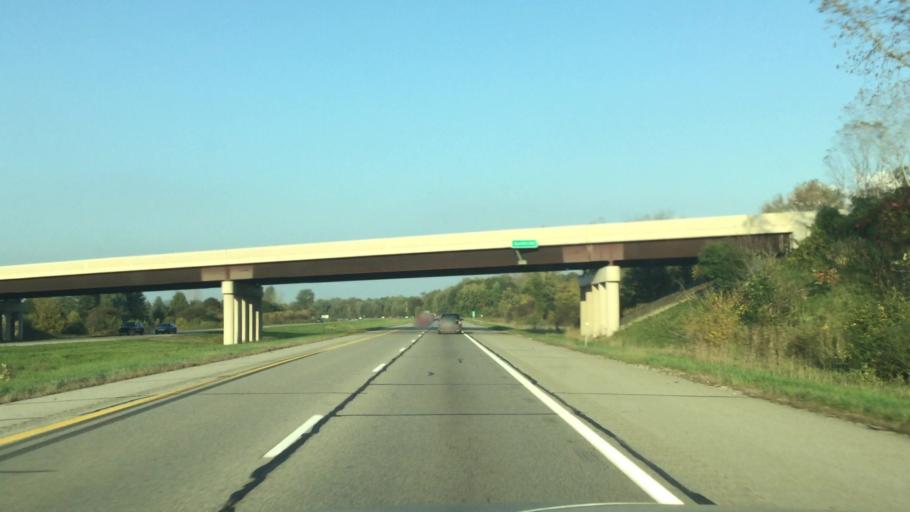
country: US
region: Michigan
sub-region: Washtenaw County
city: Ypsilanti
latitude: 42.3381
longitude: -83.6066
